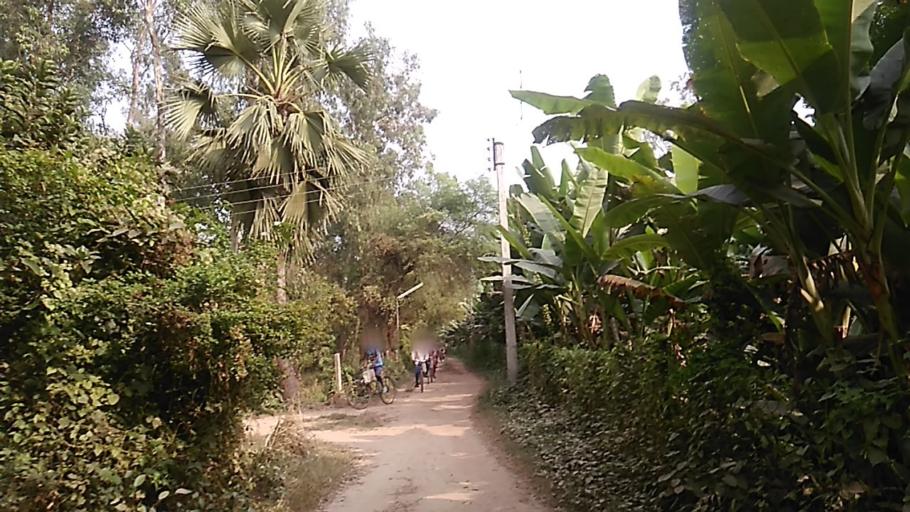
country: IN
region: West Bengal
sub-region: Nadia
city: Navadwip
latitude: 23.4259
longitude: 88.3960
